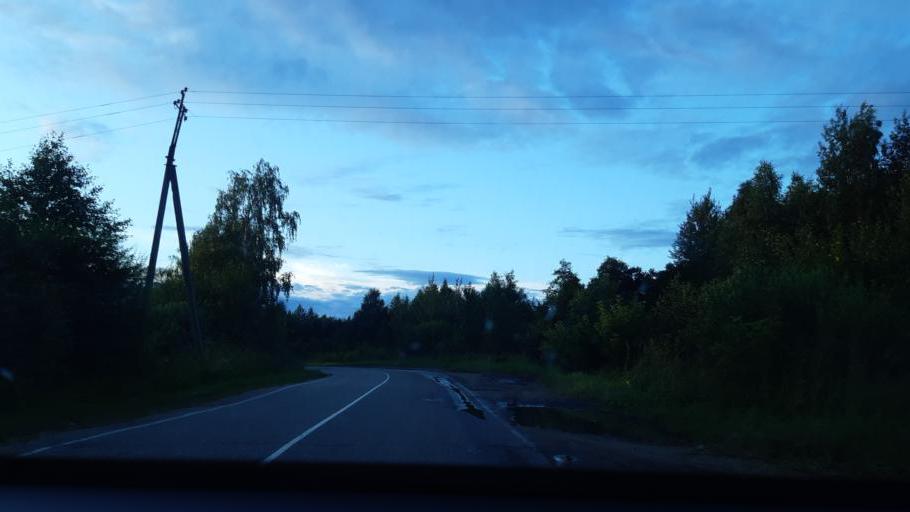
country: RU
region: Smolensk
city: Safonovo
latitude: 55.1291
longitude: 33.2004
